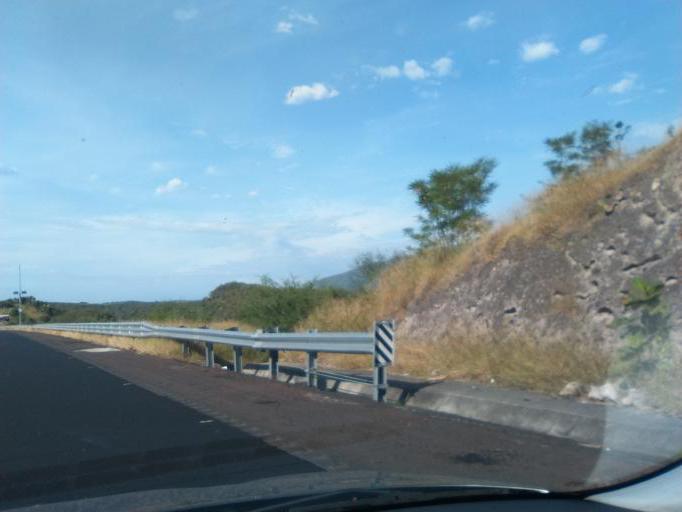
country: MX
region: Morelos
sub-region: Jojutla
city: Higueron
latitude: 18.5199
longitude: -99.1959
